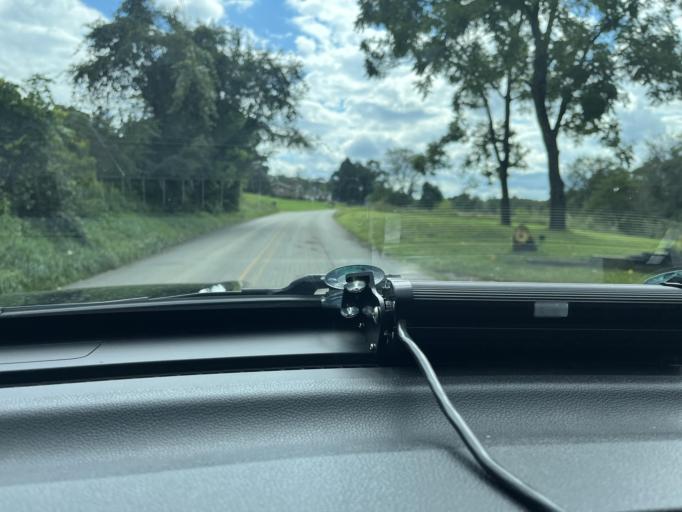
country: US
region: Pennsylvania
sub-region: Fayette County
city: South Uniontown
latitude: 39.9091
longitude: -79.7692
